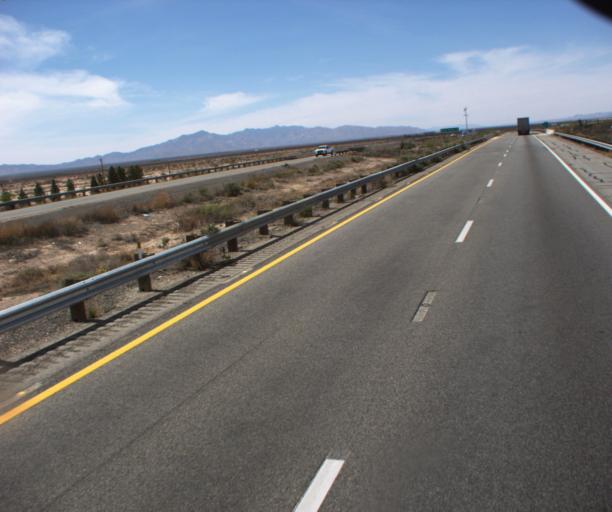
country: US
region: New Mexico
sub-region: Hidalgo County
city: Lordsburg
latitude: 32.2631
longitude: -109.2264
